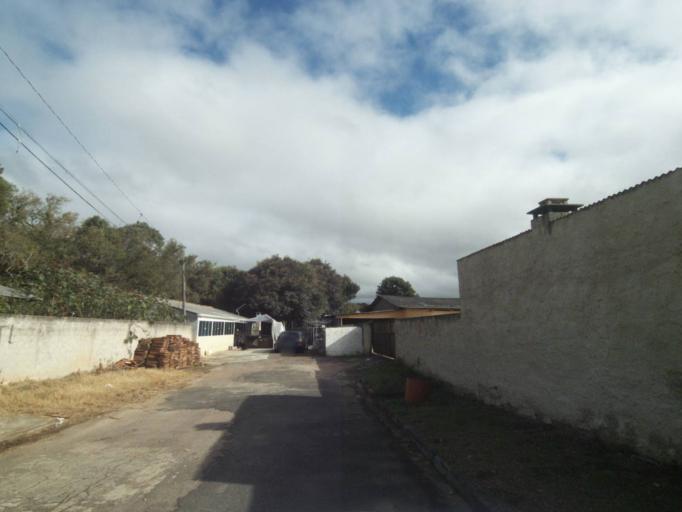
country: BR
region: Parana
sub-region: Curitiba
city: Curitiba
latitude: -25.5182
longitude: -49.3116
